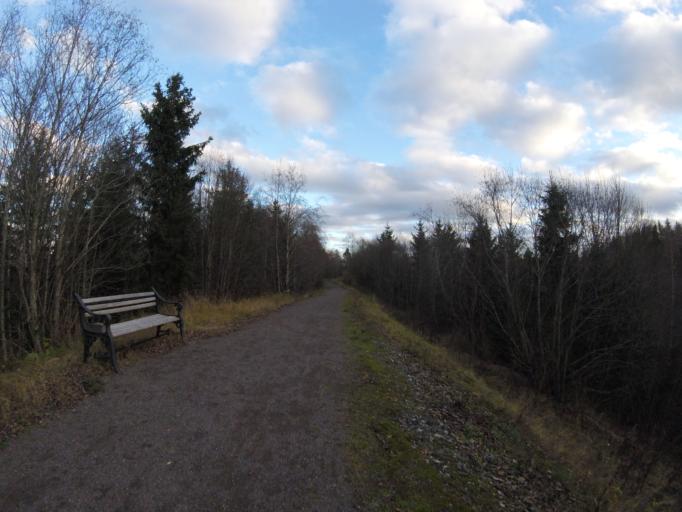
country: NO
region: Akershus
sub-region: Skedsmo
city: Leirsund
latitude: 59.9985
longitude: 11.0673
